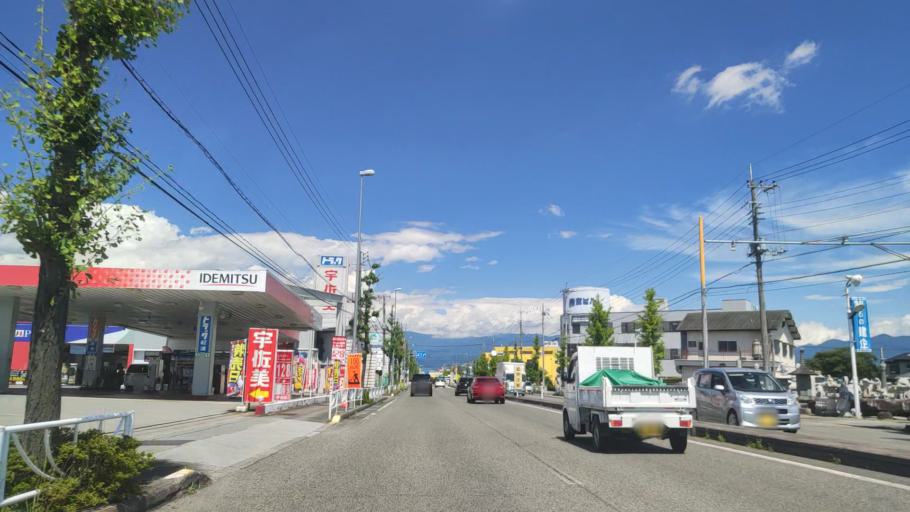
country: JP
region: Yamanashi
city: Isawa
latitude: 35.6427
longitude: 138.5985
